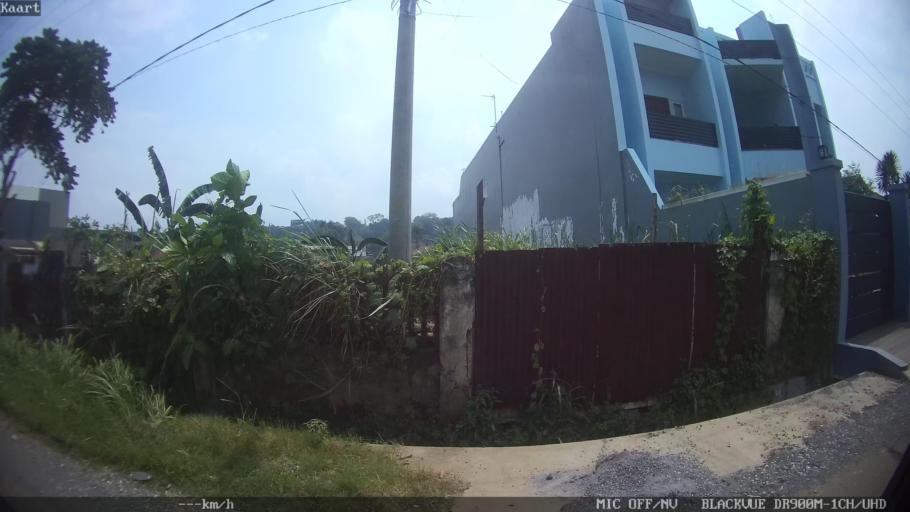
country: ID
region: Lampung
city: Bandarlampung
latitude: -5.4382
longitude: 105.2735
